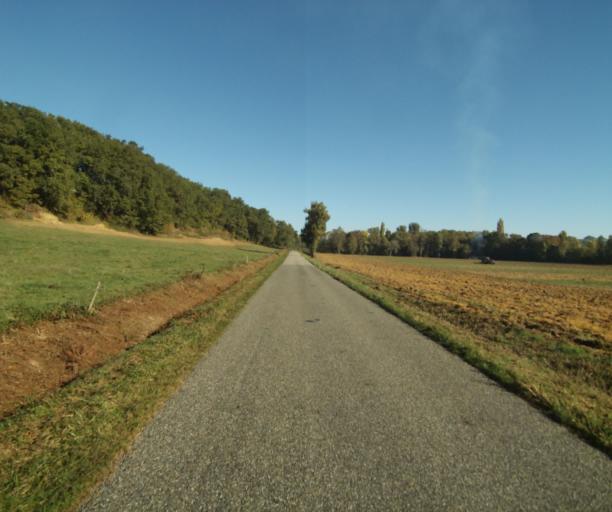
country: FR
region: Midi-Pyrenees
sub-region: Departement du Gers
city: Vic-Fezensac
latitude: 43.8226
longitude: 0.2882
